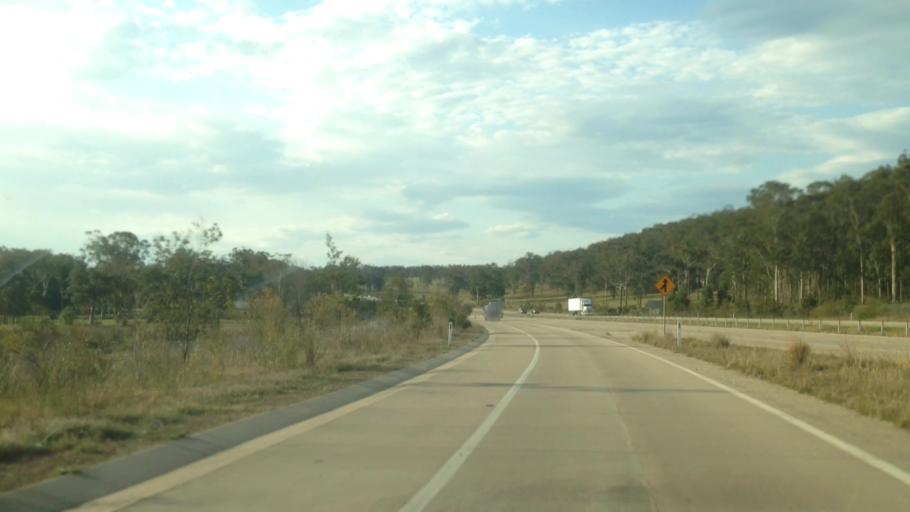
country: AU
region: New South Wales
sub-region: Cessnock
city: Heddon Greta
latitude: -32.8426
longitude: 151.5421
